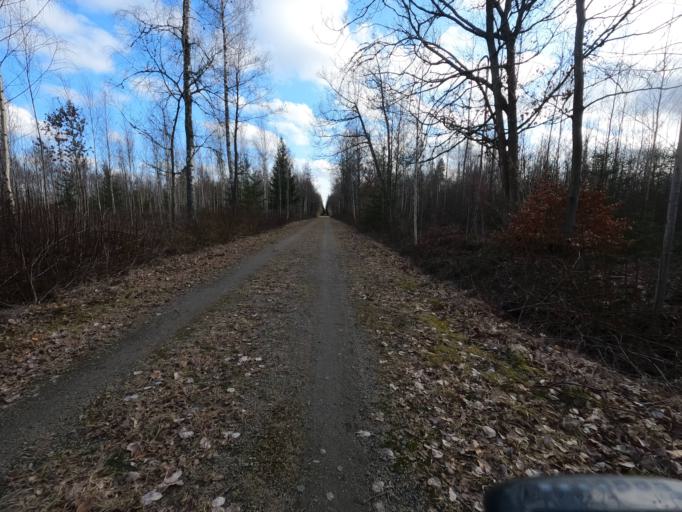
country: SE
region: Kronoberg
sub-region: Alvesta Kommun
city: Vislanda
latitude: 56.6551
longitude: 14.6185
